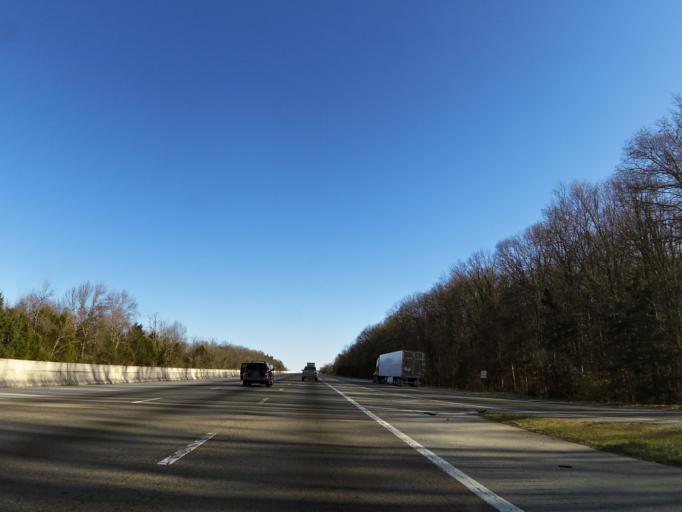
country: US
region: Tennessee
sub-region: Jefferson County
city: Dandridge
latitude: 36.0535
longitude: -83.4105
